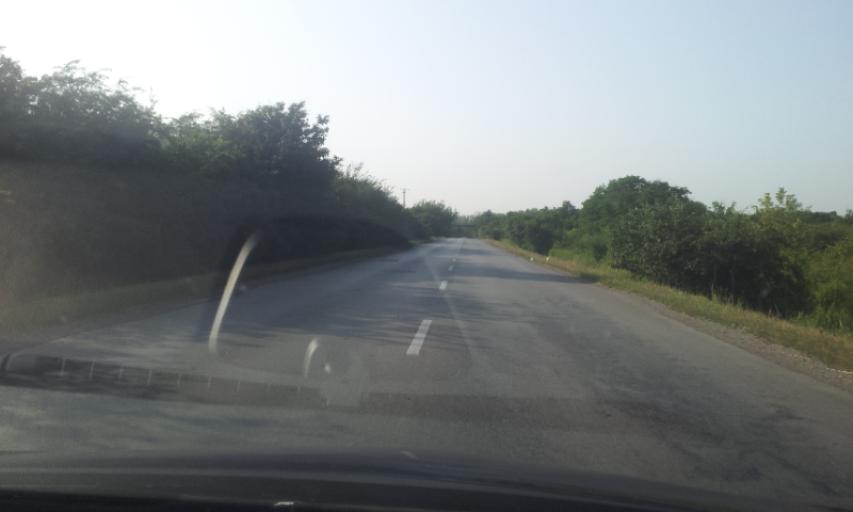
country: SK
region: Kosicky
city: Kosice
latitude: 48.6251
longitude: 21.2237
